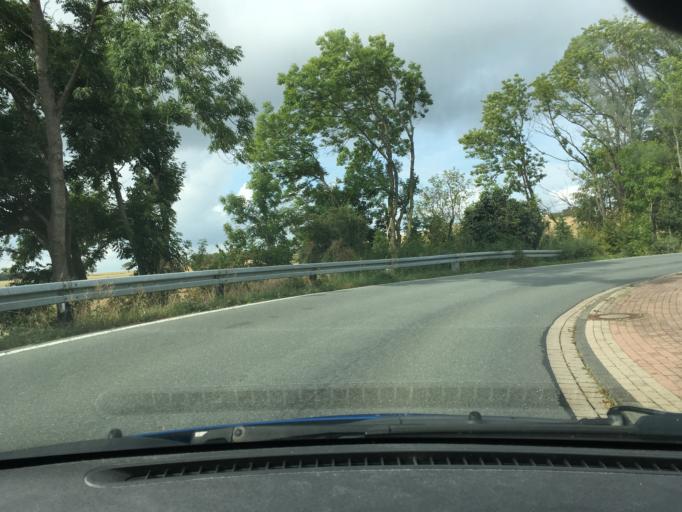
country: DE
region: Lower Saxony
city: Messenkamp
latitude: 52.2396
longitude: 9.4263
